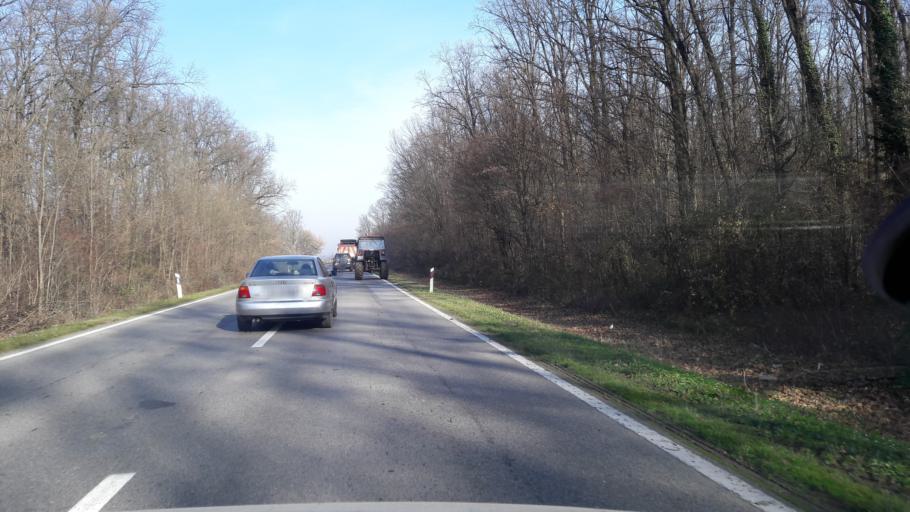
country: HR
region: Vukovarsko-Srijemska
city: Gradiste
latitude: 45.1301
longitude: 18.7171
